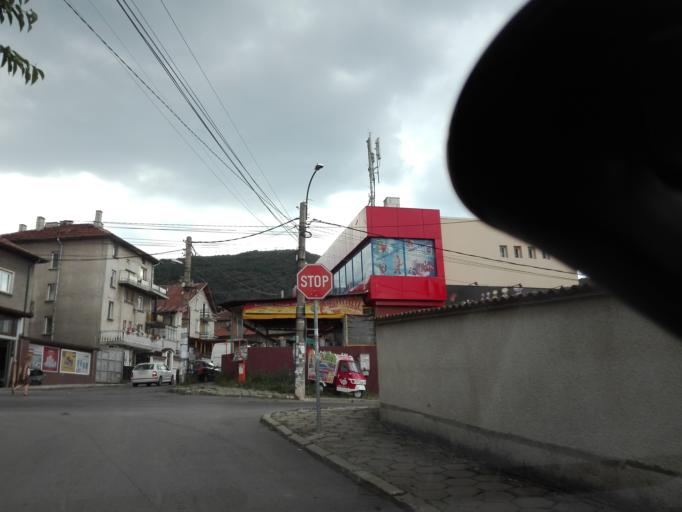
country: BG
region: Sofiya
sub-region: Obshtina Elin Pelin
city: Elin Pelin
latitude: 42.6018
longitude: 23.4827
